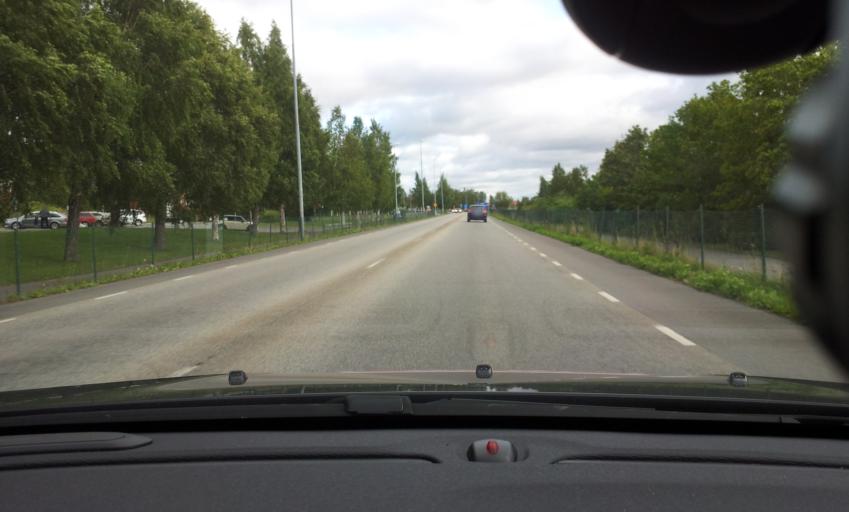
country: SE
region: Jaemtland
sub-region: OEstersunds Kommun
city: Ostersund
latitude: 63.1569
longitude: 14.6772
